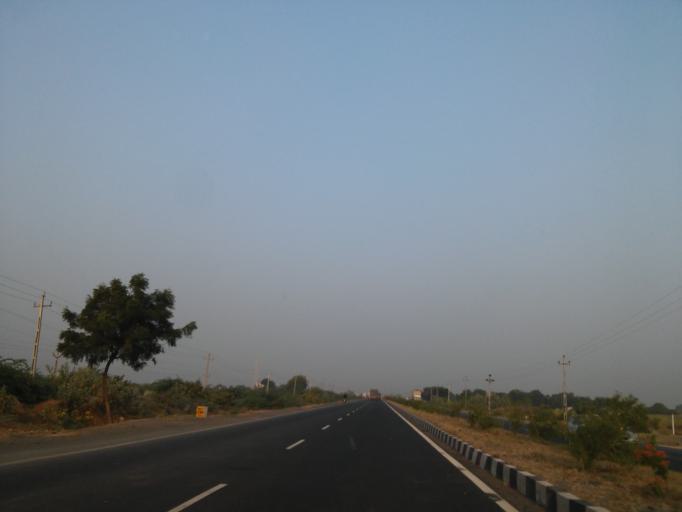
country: IN
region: Gujarat
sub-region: Kachchh
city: Bhachau
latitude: 23.2883
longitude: 70.5835
